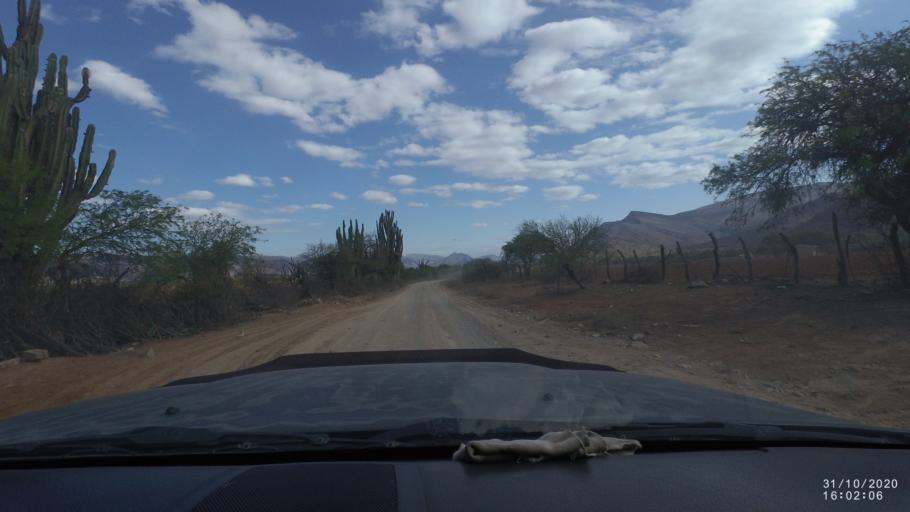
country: BO
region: Chuquisaca
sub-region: Provincia Zudanez
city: Mojocoya
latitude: -18.3447
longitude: -64.6577
